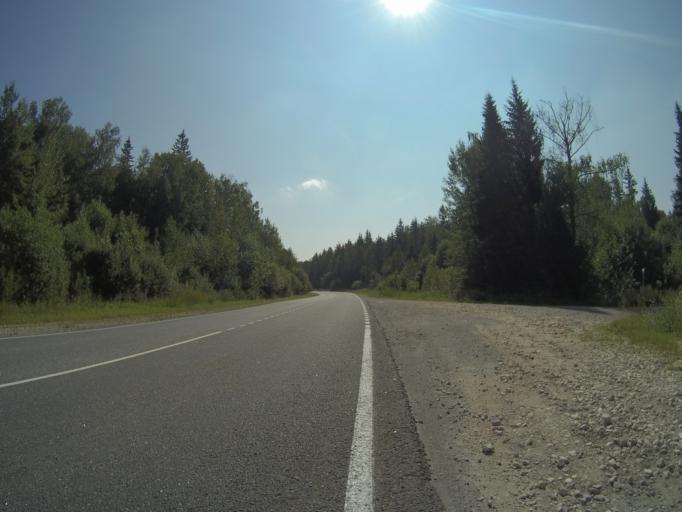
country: RU
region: Vladimir
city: Anopino
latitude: 55.7487
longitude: 40.6741
